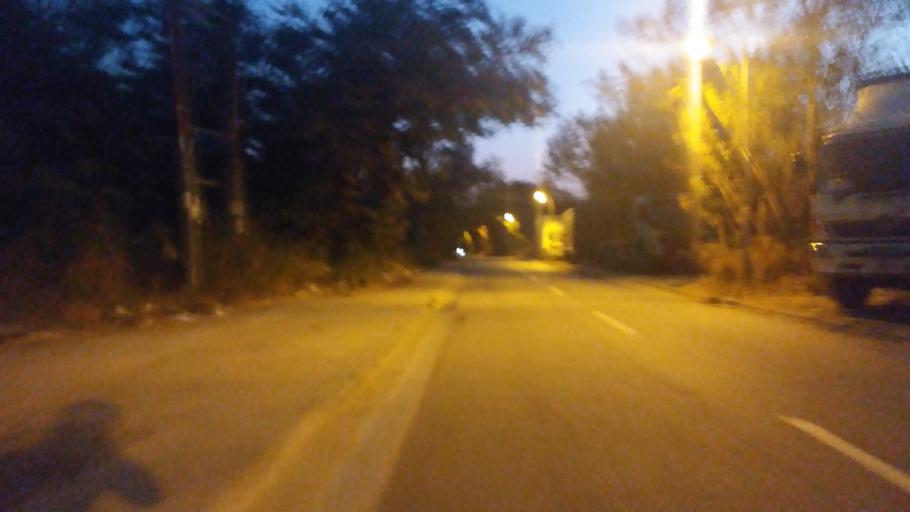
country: HK
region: Yuen Long
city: Yuen Long Kau Hui
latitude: 22.4457
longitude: 113.9974
